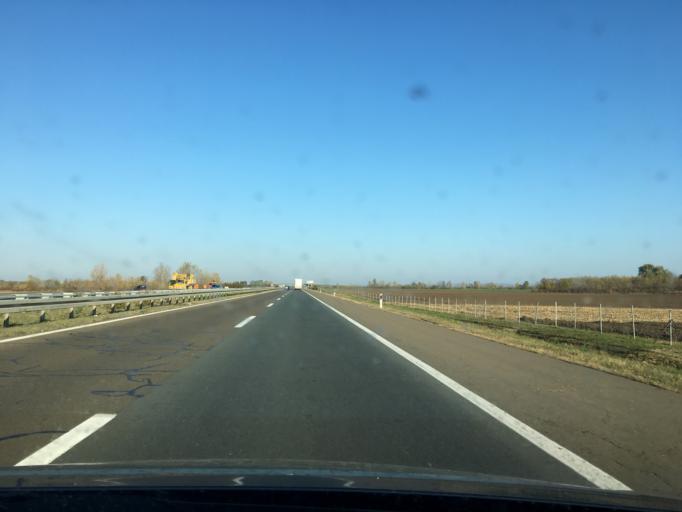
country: RS
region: Autonomna Pokrajina Vojvodina
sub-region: Sremski Okrug
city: Stara Pazova
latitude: 45.0179
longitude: 20.1950
